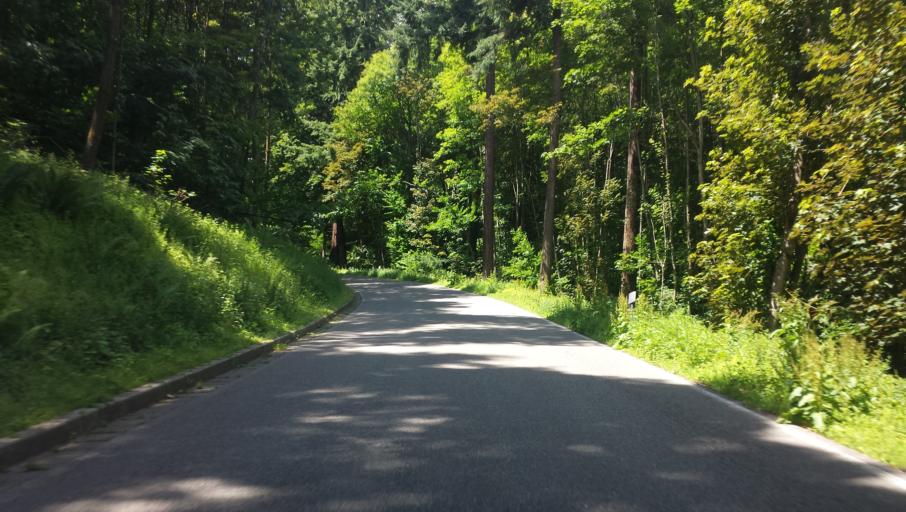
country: DE
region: Rheinland-Pfalz
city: Annweiler am Trifels
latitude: 49.1878
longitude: 7.9659
